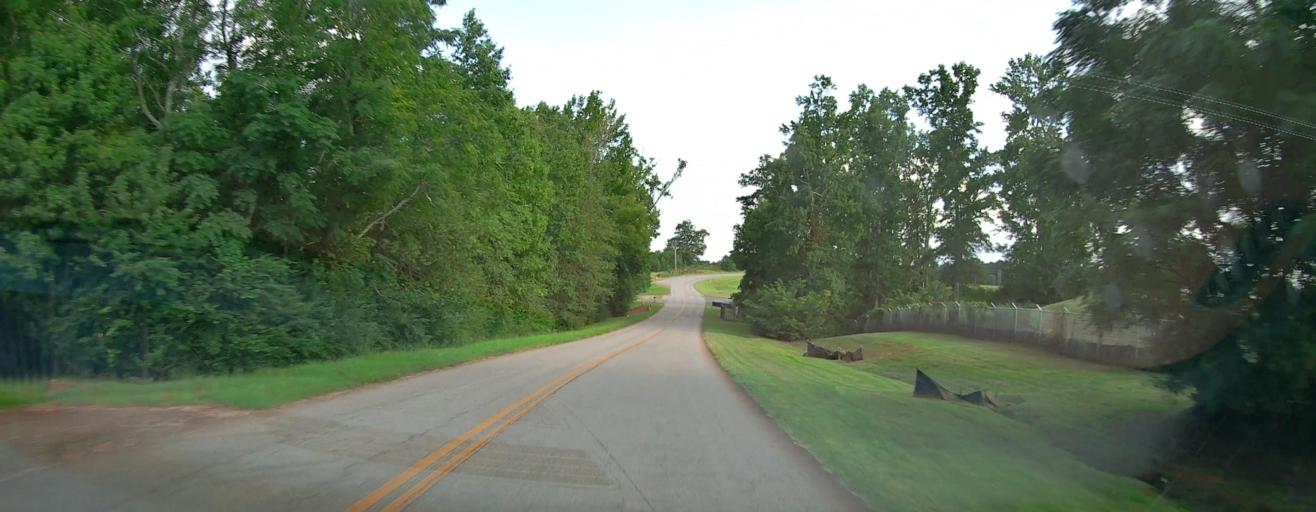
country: US
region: Georgia
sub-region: Monroe County
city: Forsyth
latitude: 33.0212
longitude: -83.9127
